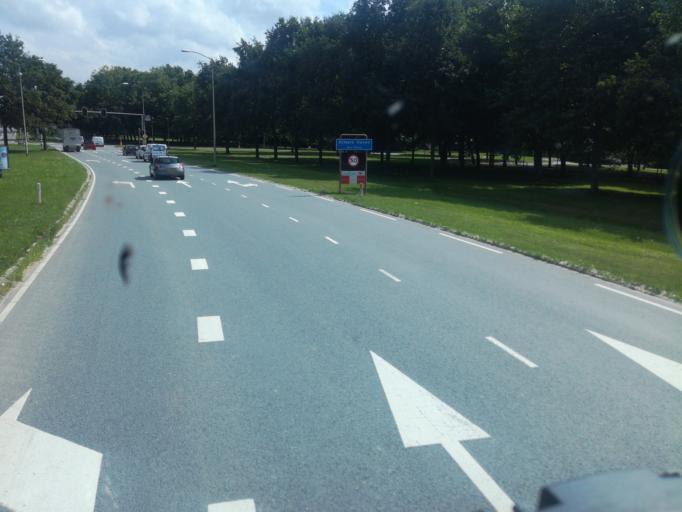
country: NL
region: Flevoland
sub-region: Gemeente Almere
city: Almere Stad
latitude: 52.3509
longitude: 5.2169
